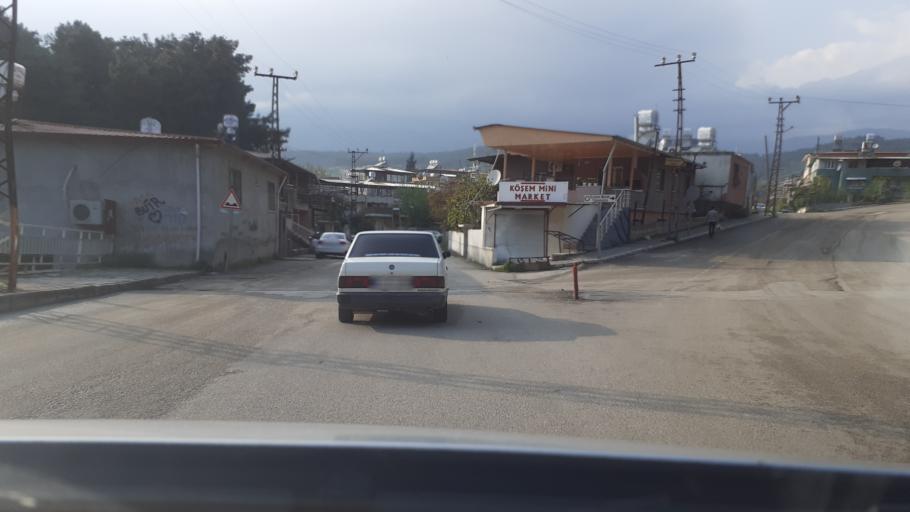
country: TR
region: Hatay
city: Kirikhan
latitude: 36.4987
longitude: 36.3437
